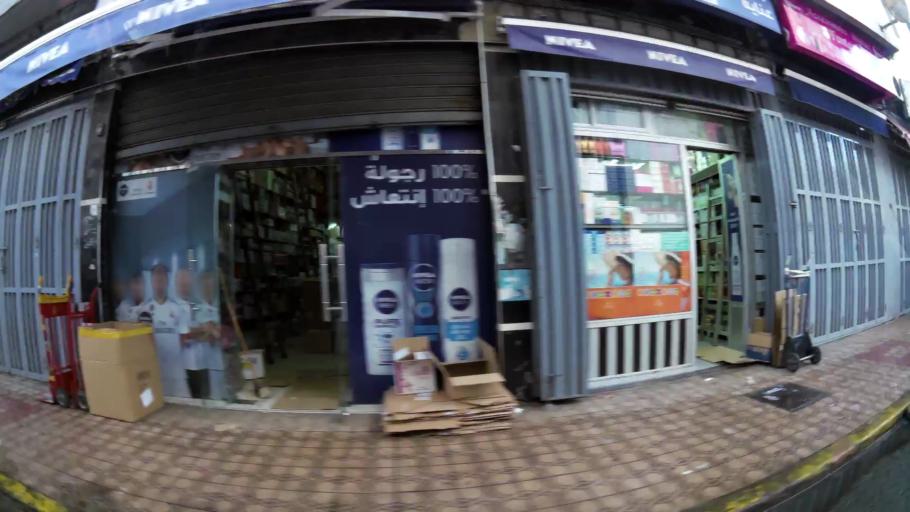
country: MA
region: Grand Casablanca
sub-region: Casablanca
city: Casablanca
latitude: 33.5866
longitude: -7.6091
